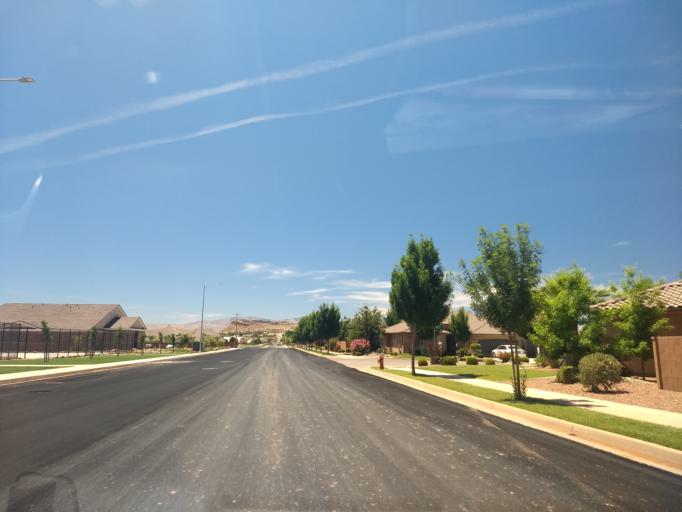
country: US
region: Utah
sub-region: Washington County
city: Washington
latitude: 37.0743
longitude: -113.5091
